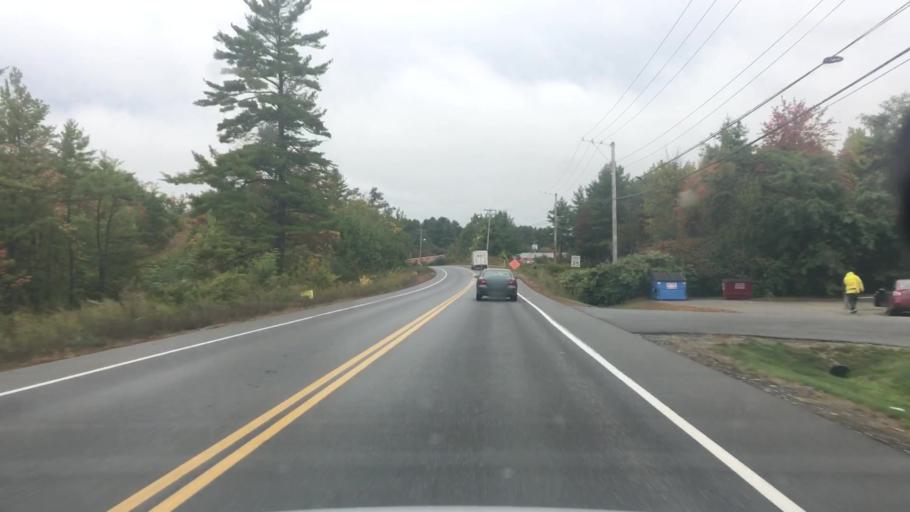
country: US
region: Maine
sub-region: Kennebec County
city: Augusta
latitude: 44.3670
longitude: -69.7888
